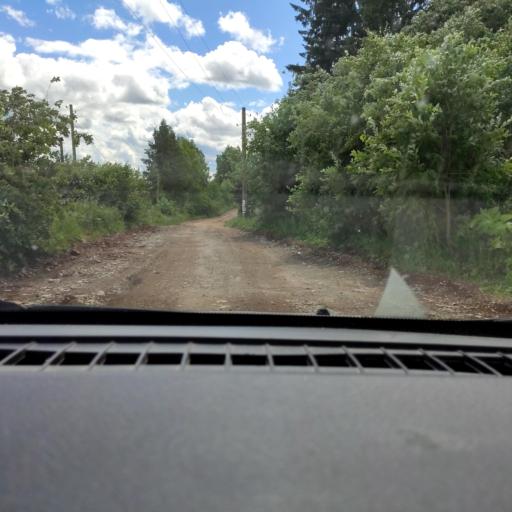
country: RU
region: Perm
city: Overyata
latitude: 58.1365
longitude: 55.8235
